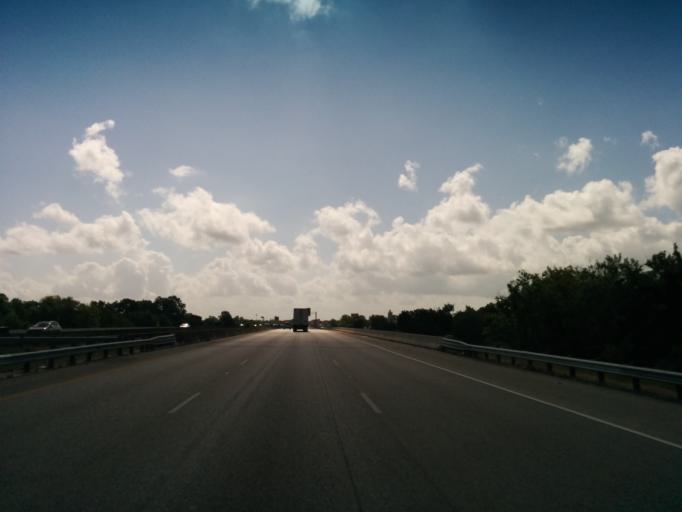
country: US
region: Texas
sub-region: Colorado County
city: Columbus
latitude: 29.6934
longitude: -96.5576
